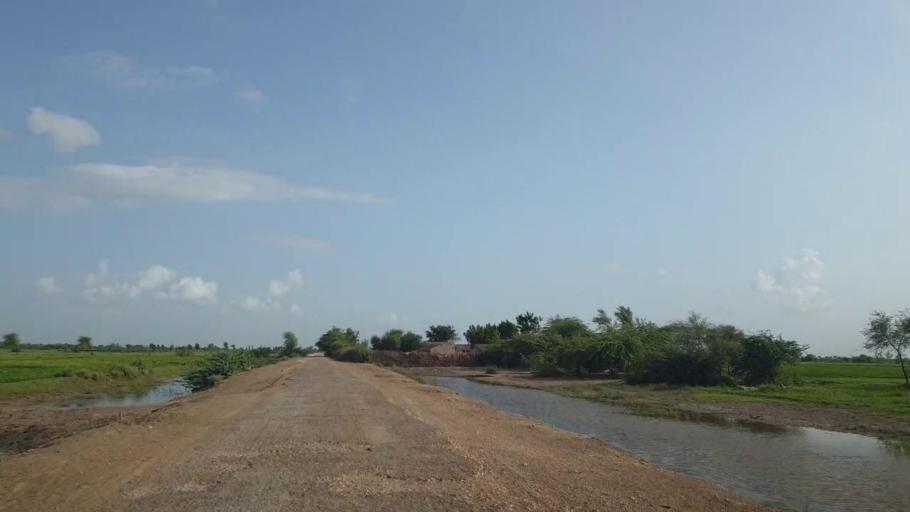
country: PK
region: Sindh
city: Kadhan
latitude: 24.6384
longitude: 69.0960
